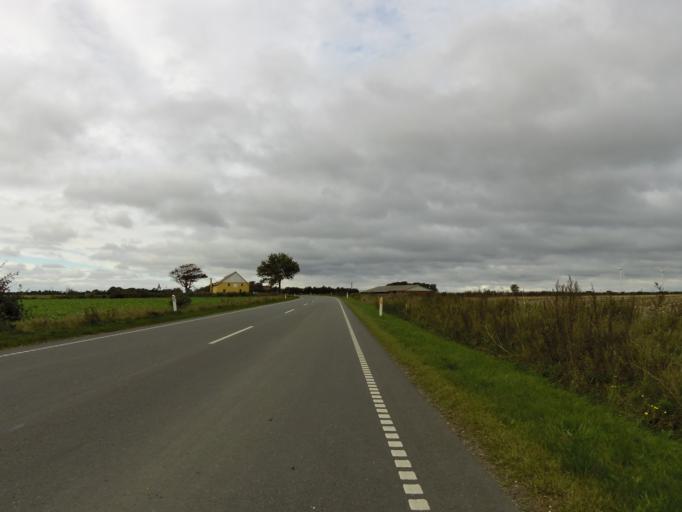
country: DK
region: South Denmark
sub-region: Tonder Kommune
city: Sherrebek
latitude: 55.2145
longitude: 8.8668
